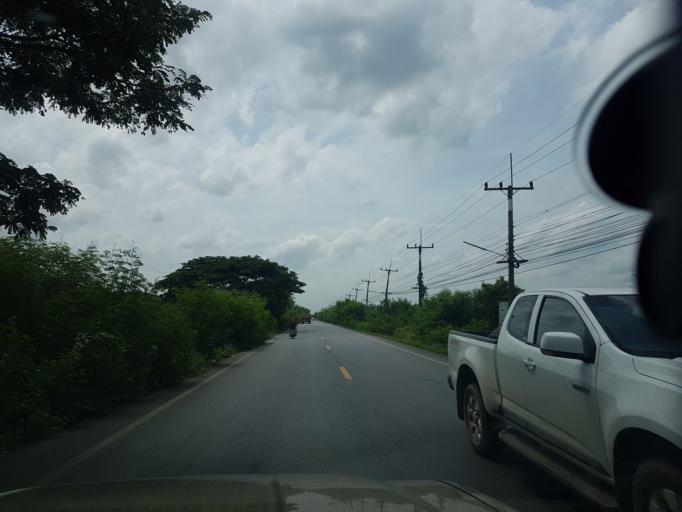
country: TH
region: Sara Buri
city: Nong Khae
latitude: 14.3165
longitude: 100.8833
